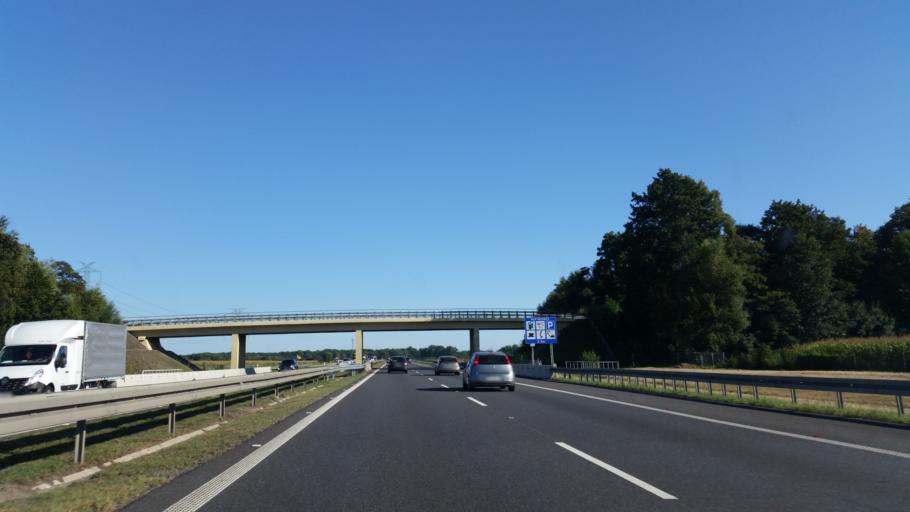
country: PL
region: Lower Silesian Voivodeship
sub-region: Powiat strzelinski
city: Wiazow
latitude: 50.8584
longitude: 17.2256
